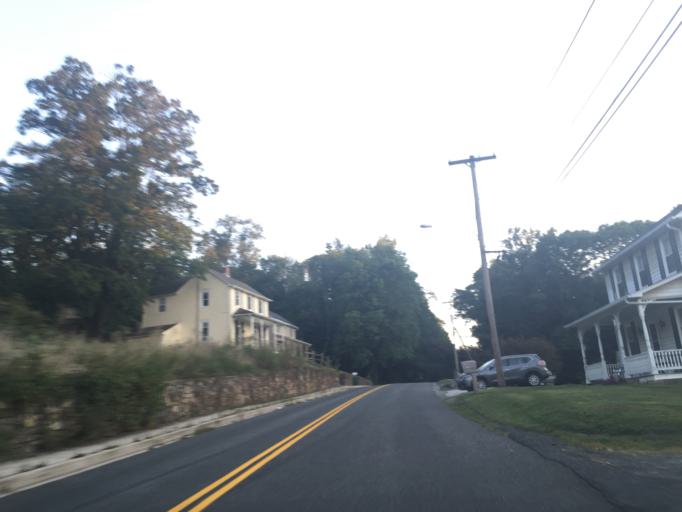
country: US
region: Pennsylvania
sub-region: York County
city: Susquehanna Trails
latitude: 39.7157
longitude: -76.3385
